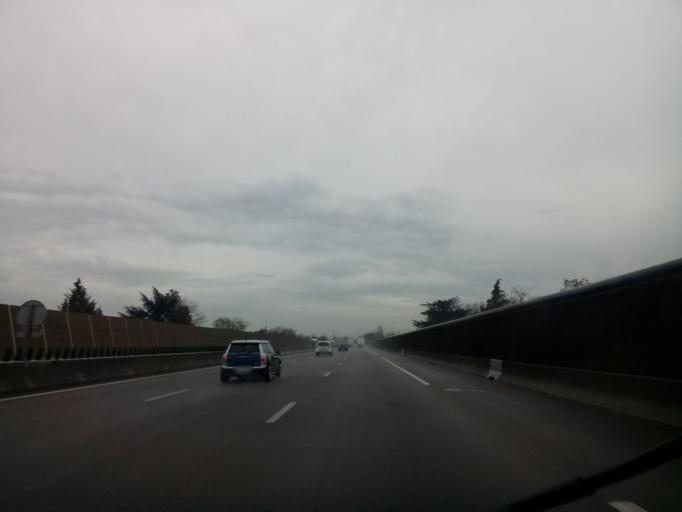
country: FR
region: Rhone-Alpes
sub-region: Departement de l'Isere
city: Roussillon
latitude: 45.3616
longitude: 4.8060
